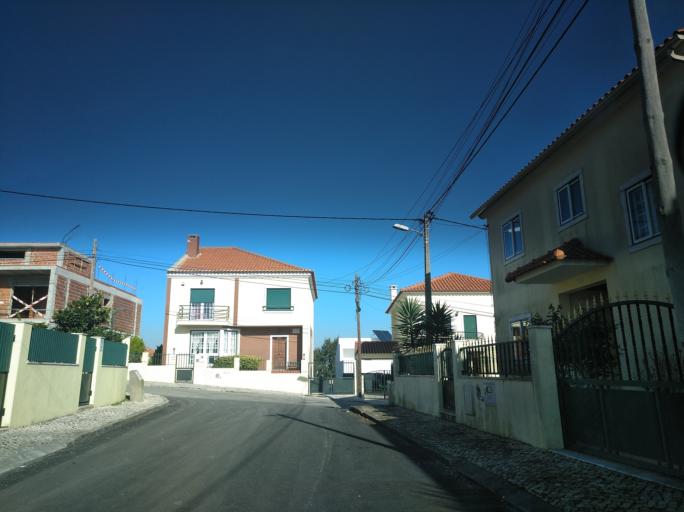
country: PT
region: Lisbon
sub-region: Odivelas
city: Canecas
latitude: 38.8020
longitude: -9.2199
